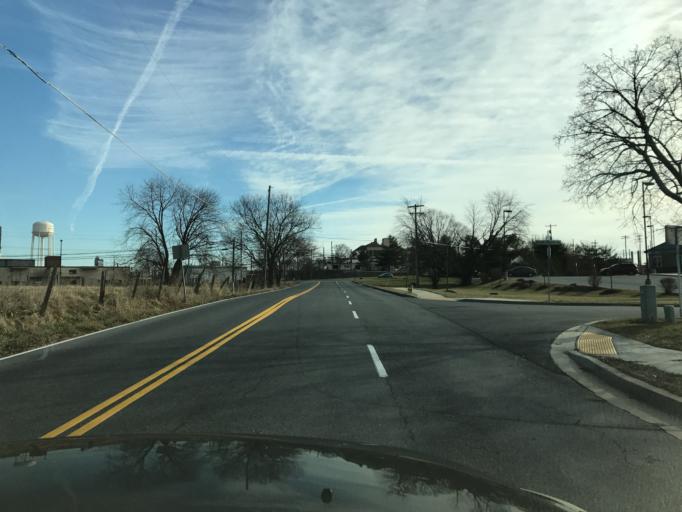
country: US
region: Maryland
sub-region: Frederick County
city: Clover Hill
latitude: 39.4362
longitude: -77.4384
